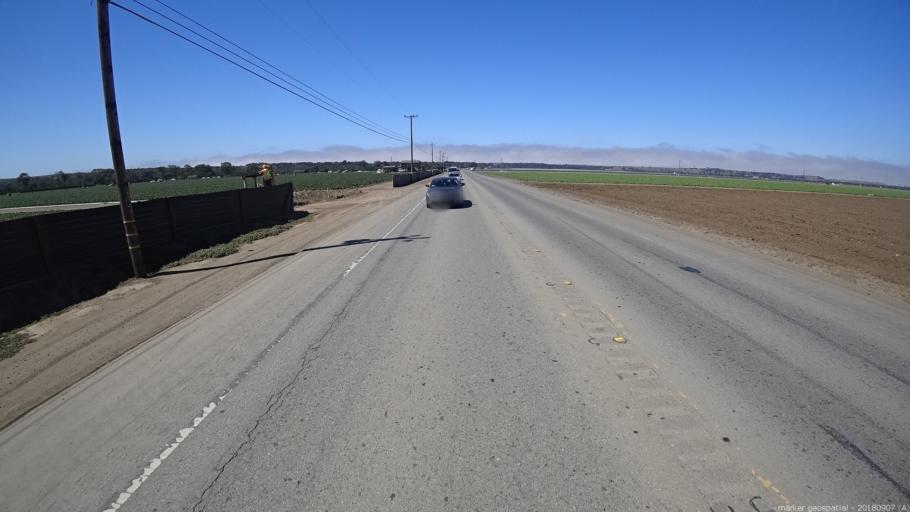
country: US
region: California
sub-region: Monterey County
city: Boronda
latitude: 36.6787
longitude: -121.7320
